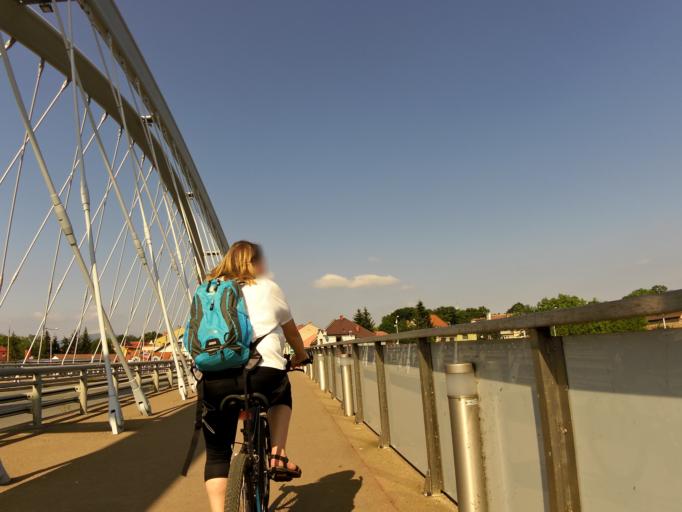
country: PL
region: Silesian Voivodeship
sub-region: Powiat zywiecki
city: Zywiec
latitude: 49.6857
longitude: 19.1931
